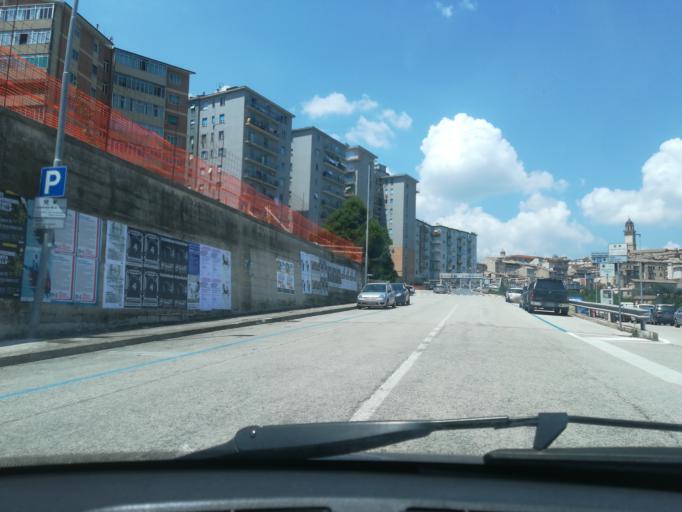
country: IT
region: The Marches
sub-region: Provincia di Macerata
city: Macerata
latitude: 43.2964
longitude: 13.4592
